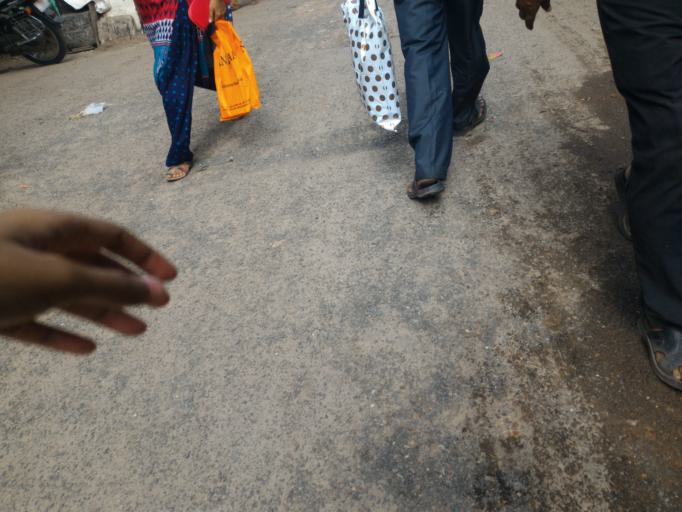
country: IN
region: Tamil Nadu
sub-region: Chennai
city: Chennai
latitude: 13.0890
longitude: 80.2788
